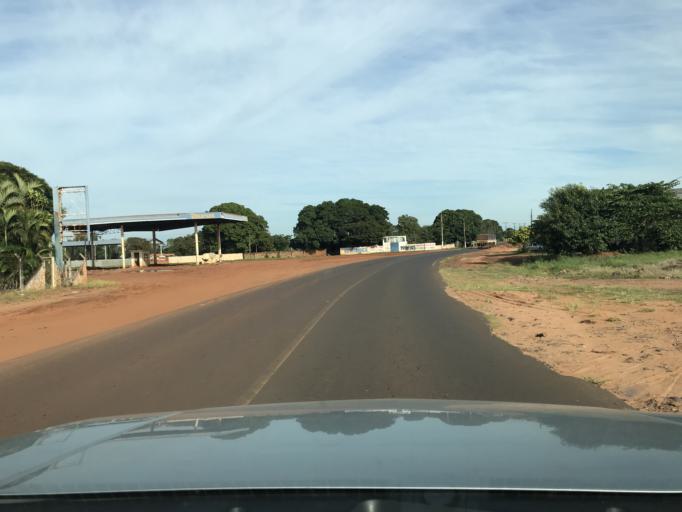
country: BR
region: Mato Grosso do Sul
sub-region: Iguatemi
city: Iguatemi
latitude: -23.6628
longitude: -54.5655
